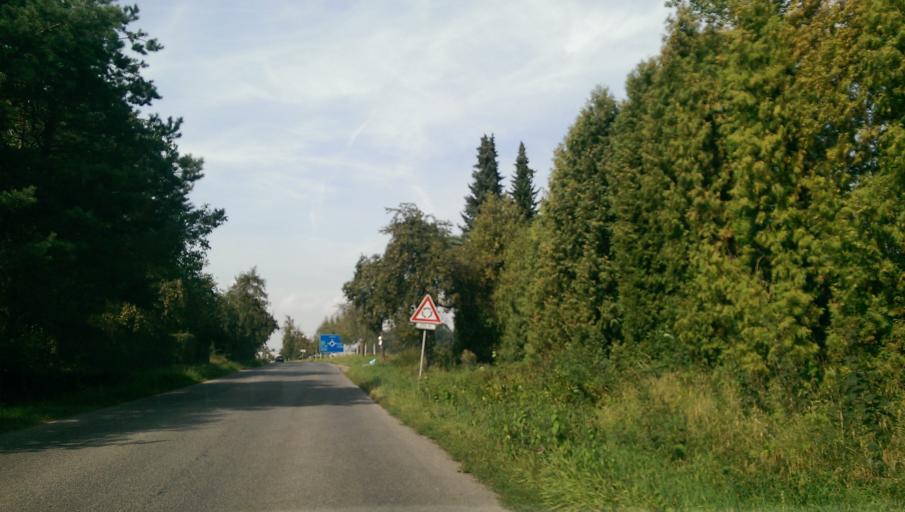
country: CZ
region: Liberecky
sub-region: Okres Semily
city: Turnov
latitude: 50.6009
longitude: 15.1543
